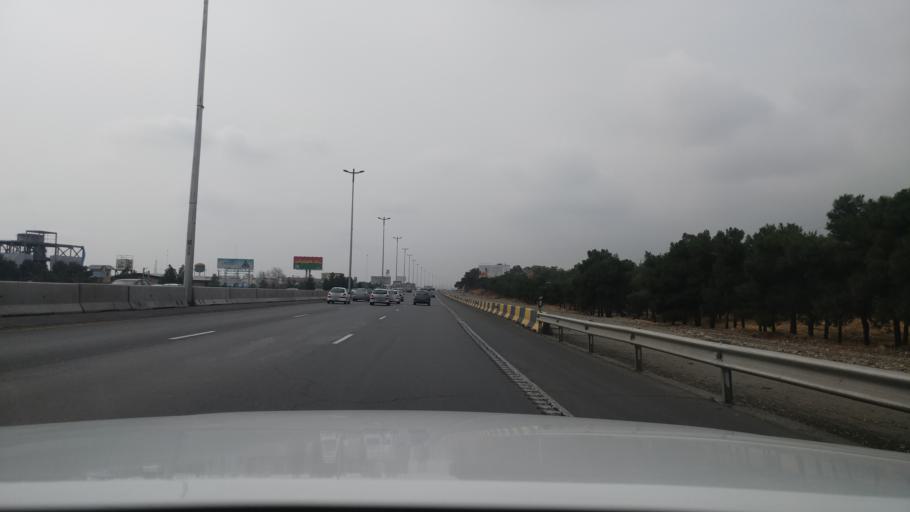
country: IR
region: Tehran
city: Shahr-e Qods
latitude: 35.7179
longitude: 51.2292
